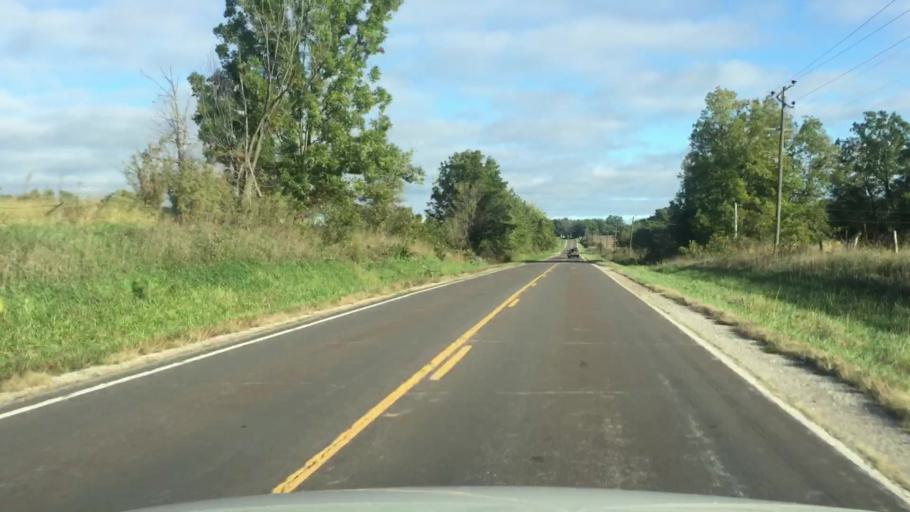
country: US
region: Missouri
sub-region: Howard County
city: New Franklin
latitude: 39.0532
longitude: -92.7444
